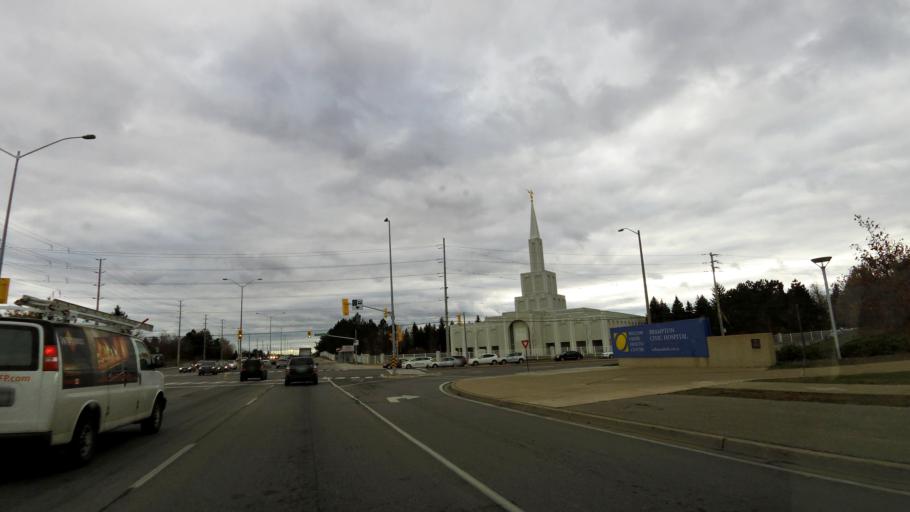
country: CA
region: Ontario
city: Brampton
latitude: 43.7450
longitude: -79.7439
